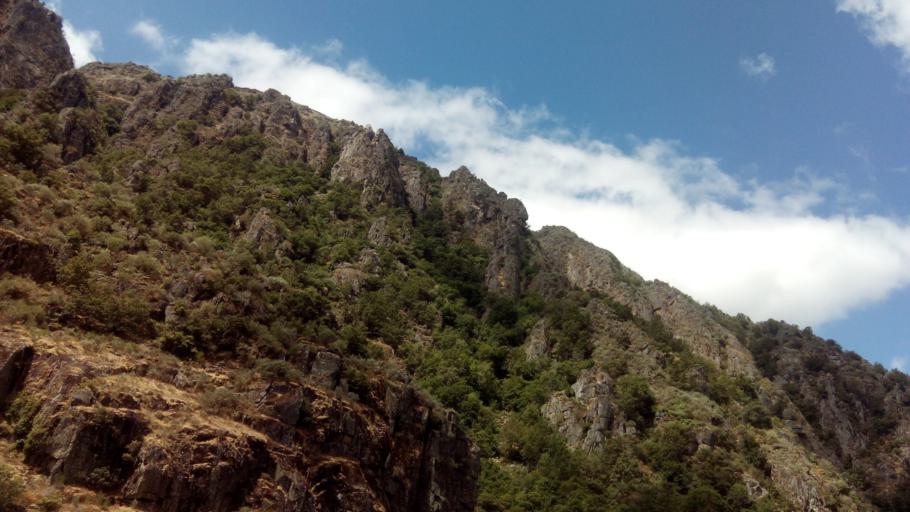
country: ES
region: Galicia
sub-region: Provincia de Lugo
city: Sober
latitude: 42.3867
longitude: -7.6200
